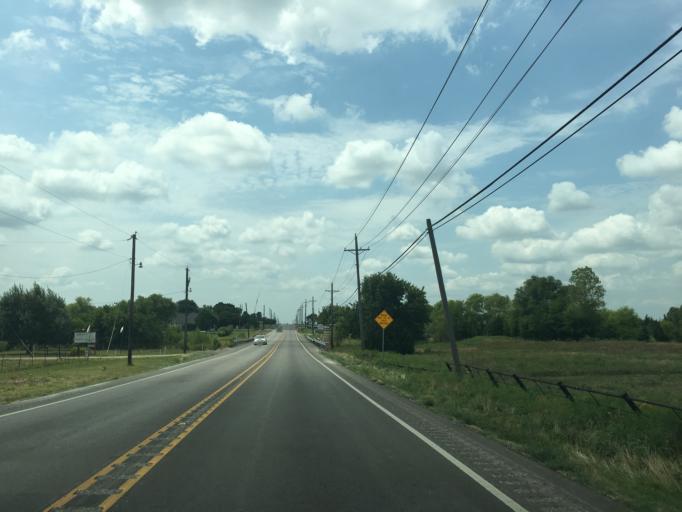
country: US
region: Texas
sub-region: Rockwall County
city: Fate
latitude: 32.9626
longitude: -96.3787
